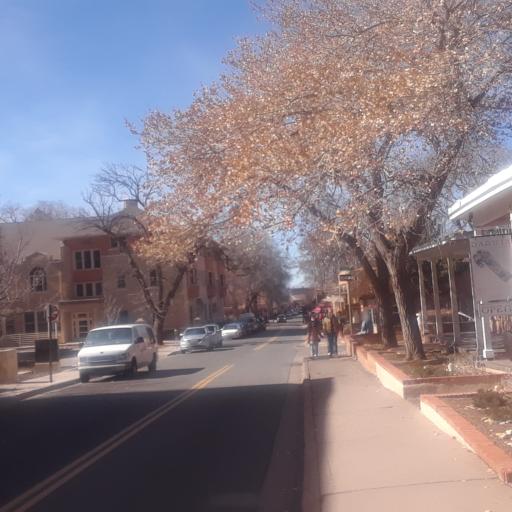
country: US
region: New Mexico
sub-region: Santa Fe County
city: Santa Fe
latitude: 35.6868
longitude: -105.9343
